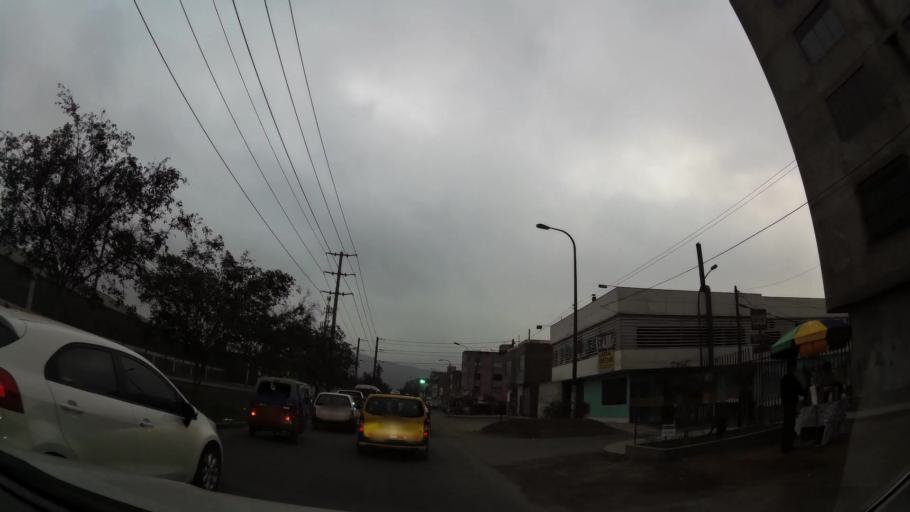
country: PE
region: Lima
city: Lima
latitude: -12.0167
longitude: -76.9966
